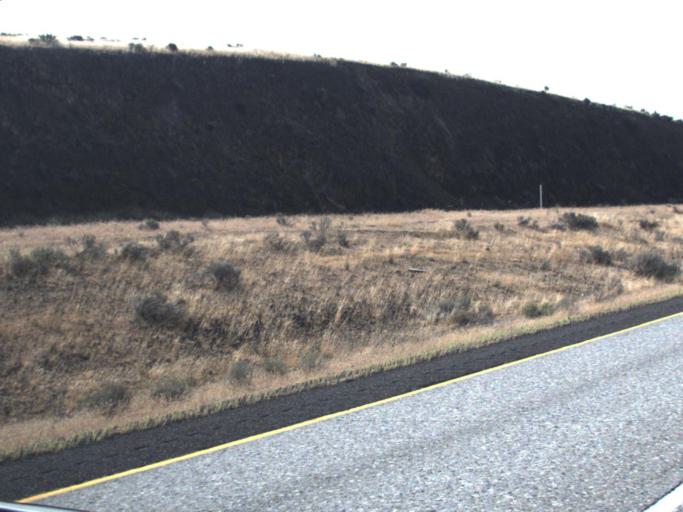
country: US
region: Washington
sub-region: Yakima County
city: Terrace Heights
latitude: 46.7651
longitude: -120.3787
